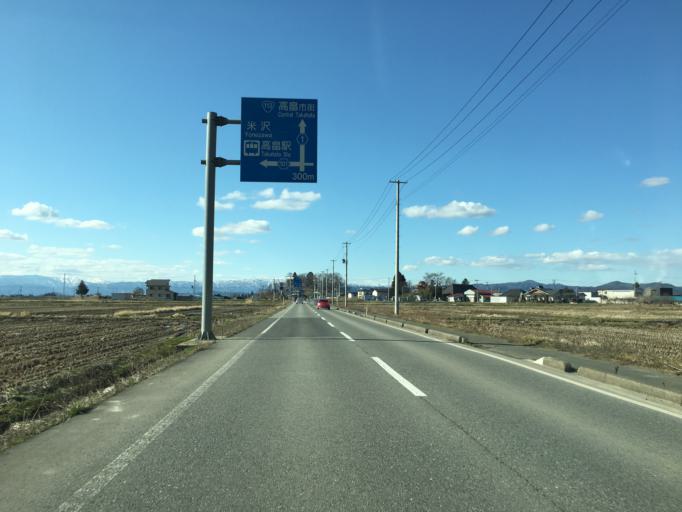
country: JP
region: Yamagata
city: Takahata
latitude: 37.9894
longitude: 140.1819
